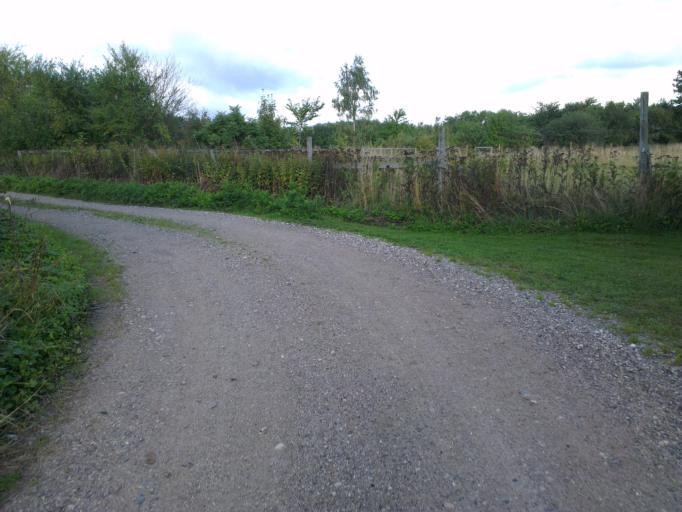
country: DK
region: Capital Region
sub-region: Frederikssund Kommune
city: Frederikssund
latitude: 55.8008
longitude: 12.0901
